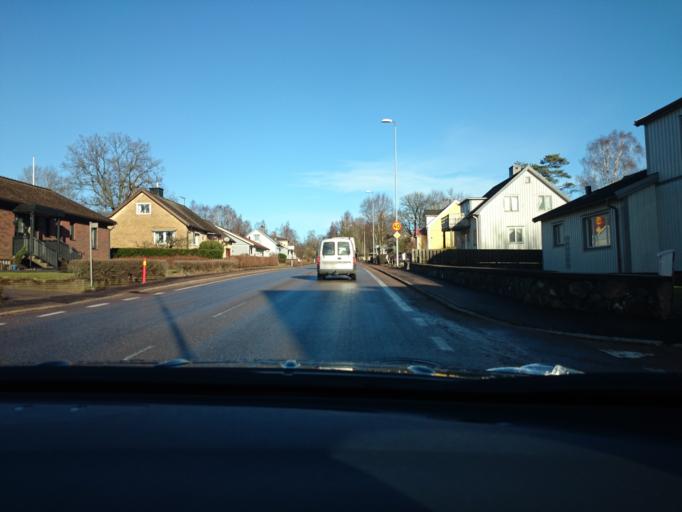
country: SE
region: Halland
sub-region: Hylte Kommun
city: Hyltebruk
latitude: 57.0086
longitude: 13.2420
